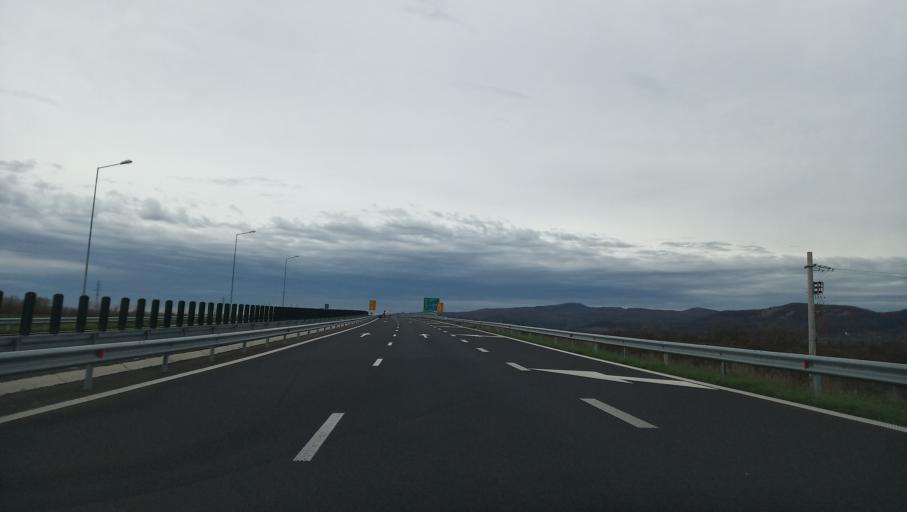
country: RO
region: Hunedoara
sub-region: Comuna Ilia
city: Ilia
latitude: 45.9482
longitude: 22.6484
